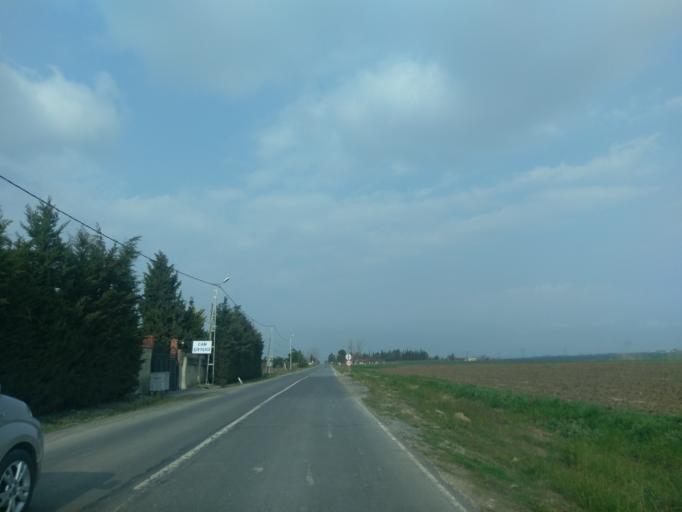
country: TR
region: Istanbul
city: Silivri
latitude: 41.0907
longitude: 28.2719
